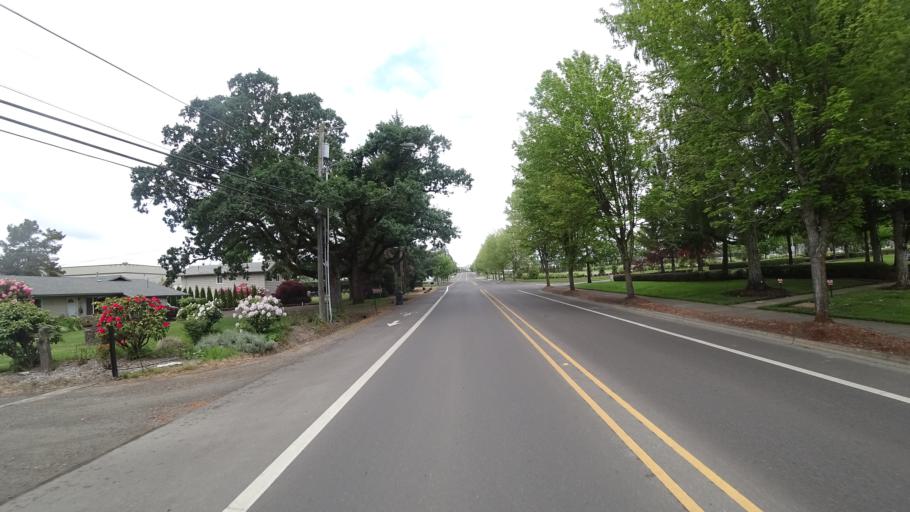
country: US
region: Oregon
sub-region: Washington County
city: Rockcreek
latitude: 45.5370
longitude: -122.8935
